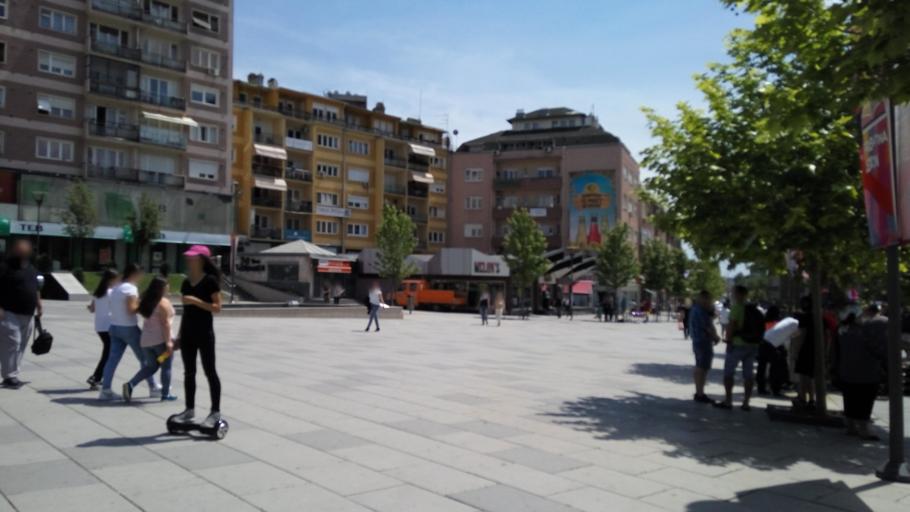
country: XK
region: Pristina
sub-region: Komuna e Prishtines
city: Pristina
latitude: 42.6603
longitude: 21.1609
